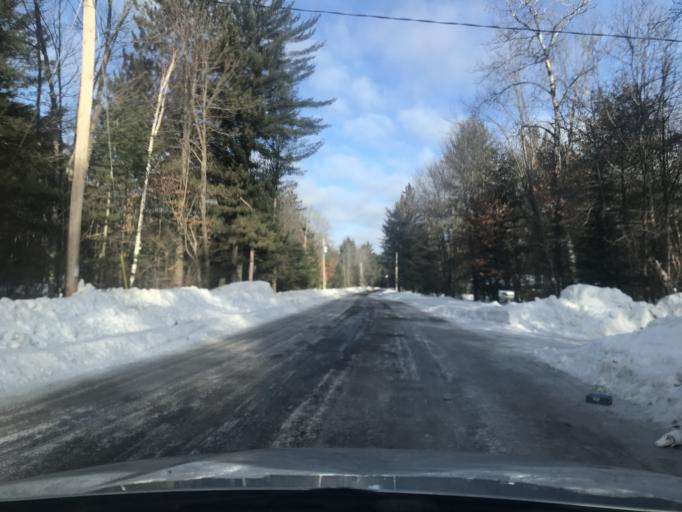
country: US
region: Wisconsin
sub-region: Marinette County
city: Niagara
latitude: 45.6351
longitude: -87.9689
